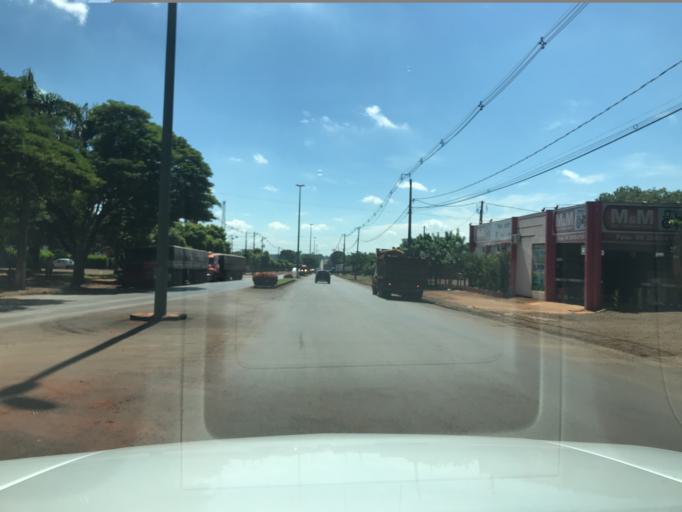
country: BR
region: Parana
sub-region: Palotina
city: Palotina
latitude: -24.2815
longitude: -53.8337
